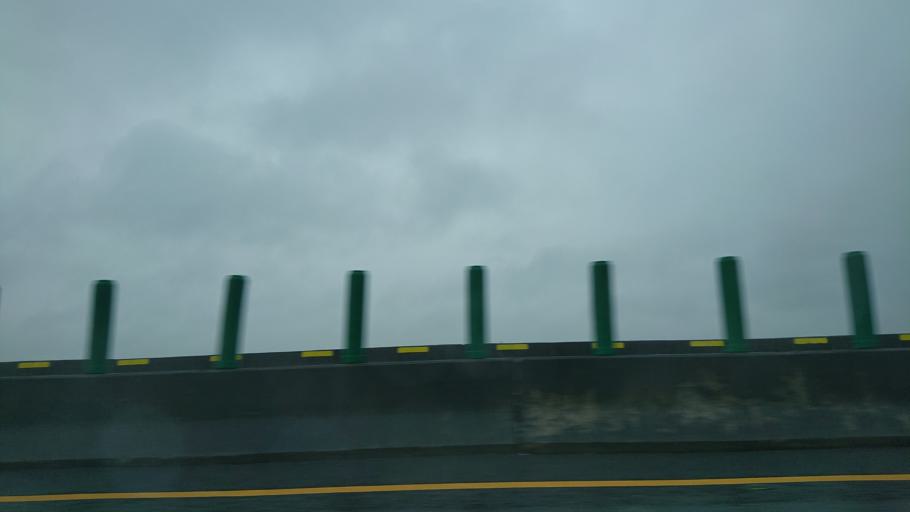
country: TW
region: Taiwan
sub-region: Chiayi
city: Taibao
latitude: 23.7132
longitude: 120.2021
